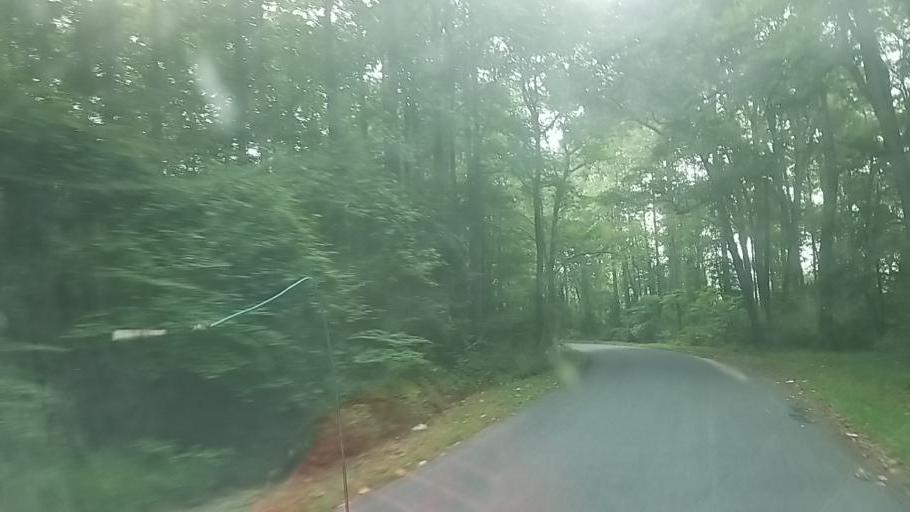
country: US
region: Maryland
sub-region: Wicomico County
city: Pittsville
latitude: 38.4417
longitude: -75.3397
